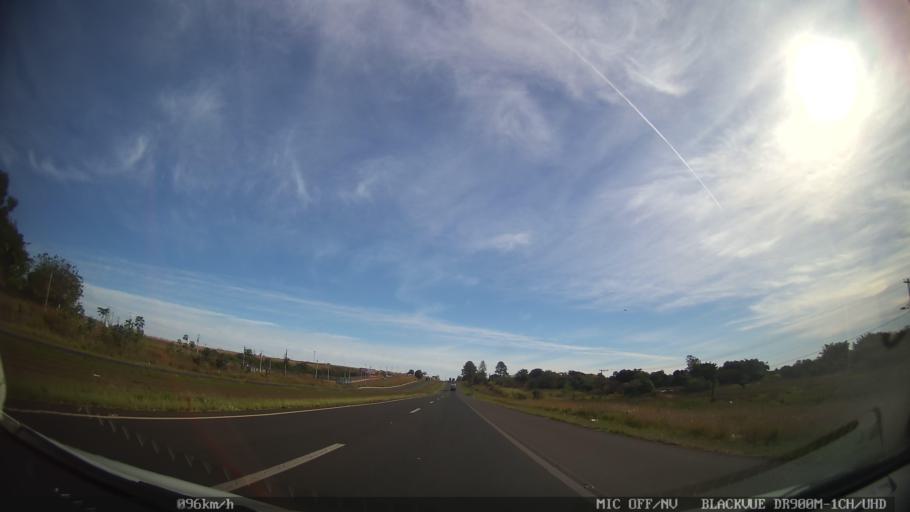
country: BR
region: Sao Paulo
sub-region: Sao Jose Do Rio Preto
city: Sao Jose do Rio Preto
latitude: -20.7966
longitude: -49.3212
